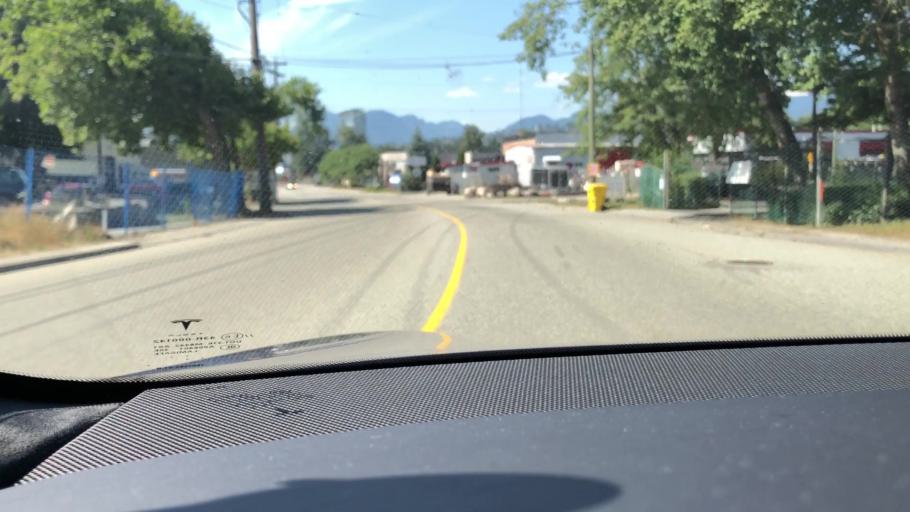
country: CA
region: British Columbia
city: Burnaby
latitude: 49.2546
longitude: -122.9751
